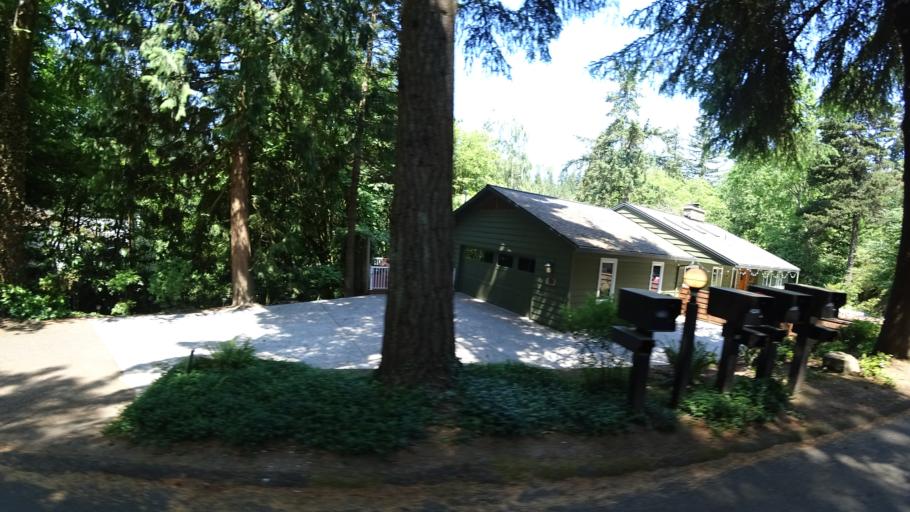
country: US
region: Oregon
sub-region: Washington County
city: West Slope
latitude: 45.5134
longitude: -122.7238
